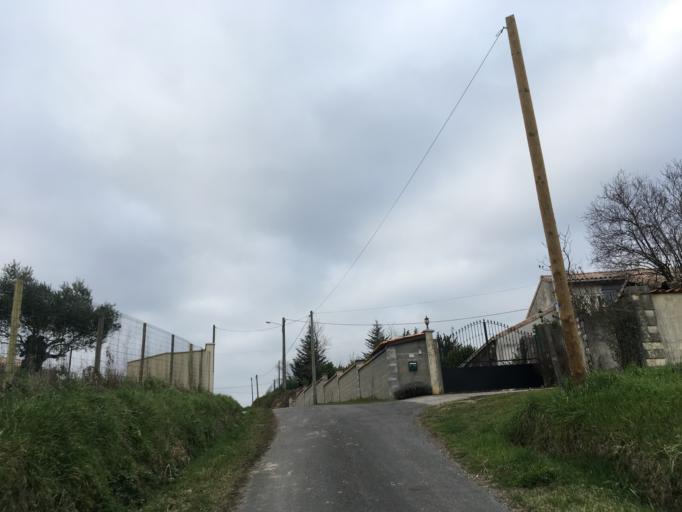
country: FR
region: Aquitaine
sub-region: Departement de la Gironde
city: Saint-Ciers-sur-Gironde
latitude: 45.3064
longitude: -0.5847
